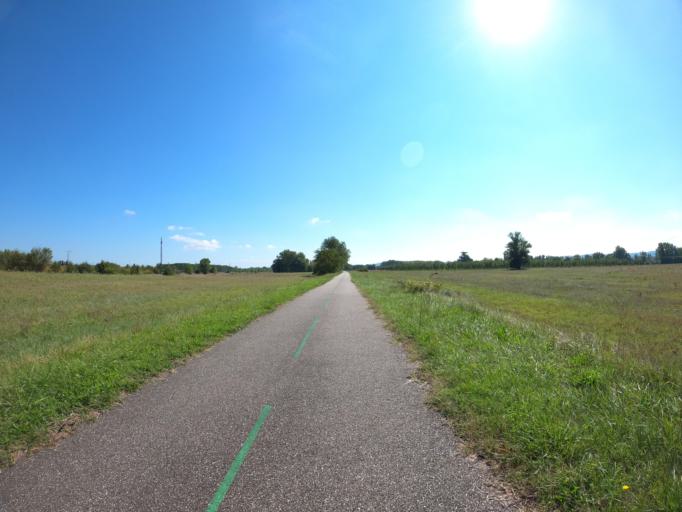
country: FR
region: Aquitaine
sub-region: Departement du Lot-et-Garonne
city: Bias
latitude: 44.4262
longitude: 0.6471
